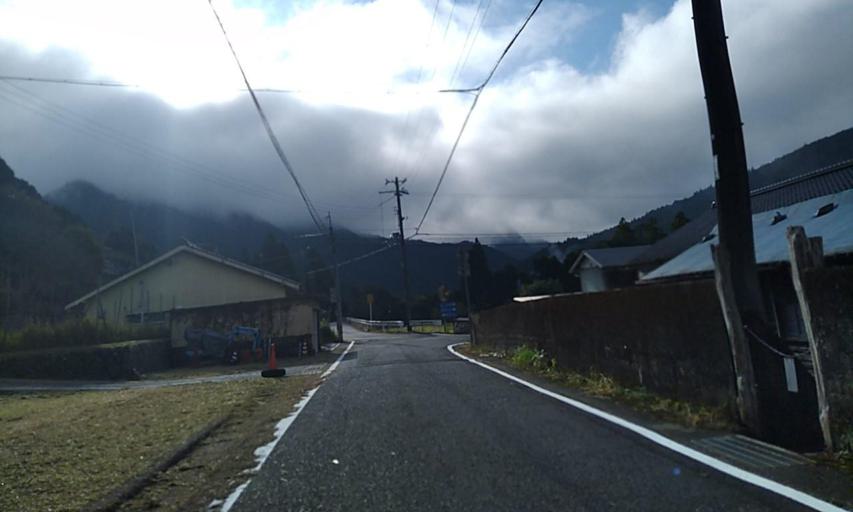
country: JP
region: Wakayama
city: Shingu
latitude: 33.9246
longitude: 135.9838
